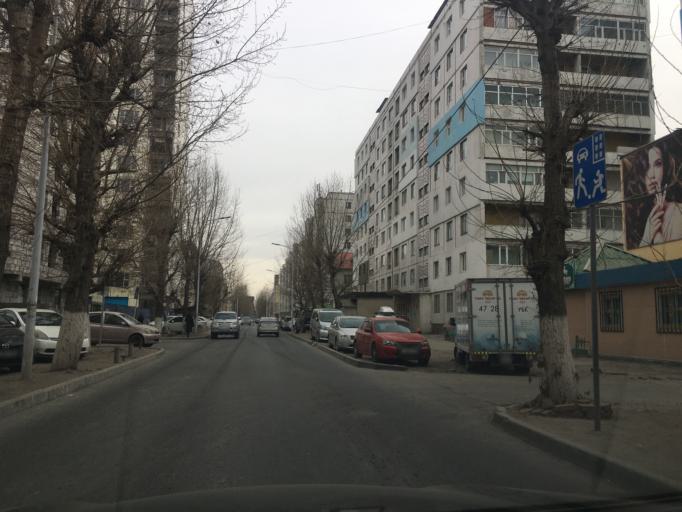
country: MN
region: Ulaanbaatar
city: Ulaanbaatar
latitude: 47.9107
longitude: 106.8881
